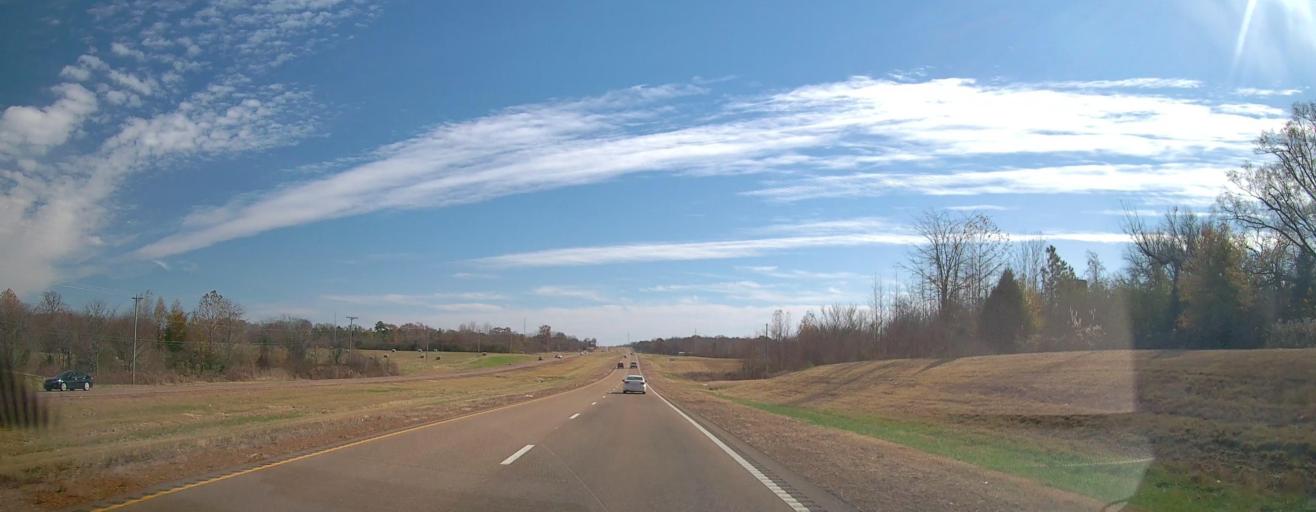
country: US
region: Tennessee
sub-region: Fayette County
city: Piperton
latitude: 34.9765
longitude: -89.5716
